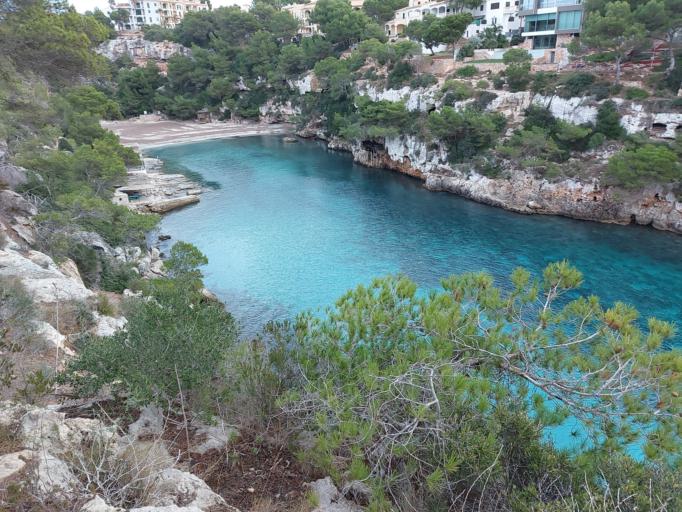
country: ES
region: Balearic Islands
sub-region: Illes Balears
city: Llucmajor
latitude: 39.3632
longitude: 2.8345
